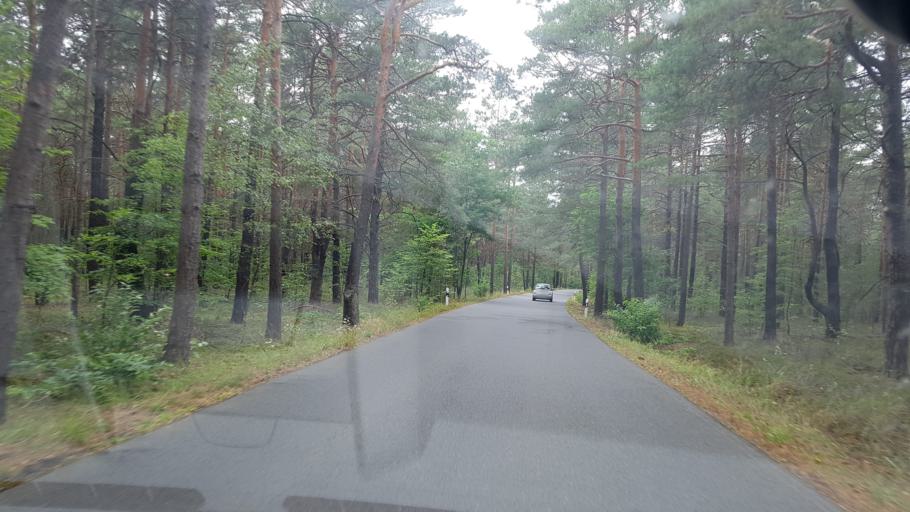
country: DE
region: Brandenburg
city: Spremberg
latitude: 51.5010
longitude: 14.4239
